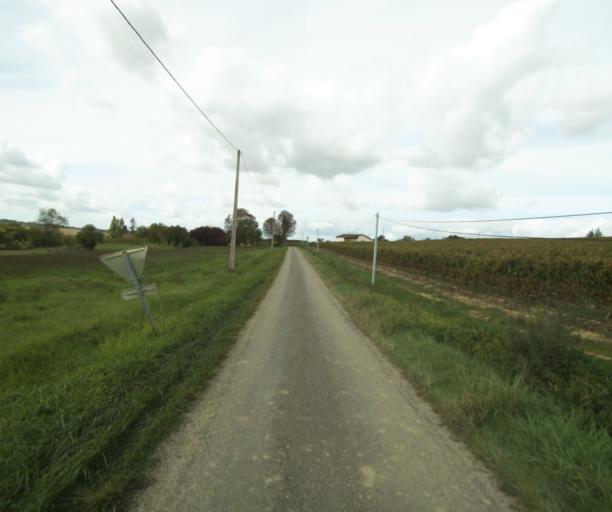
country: FR
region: Midi-Pyrenees
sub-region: Departement du Gers
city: Eauze
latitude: 43.8404
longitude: 0.0914
